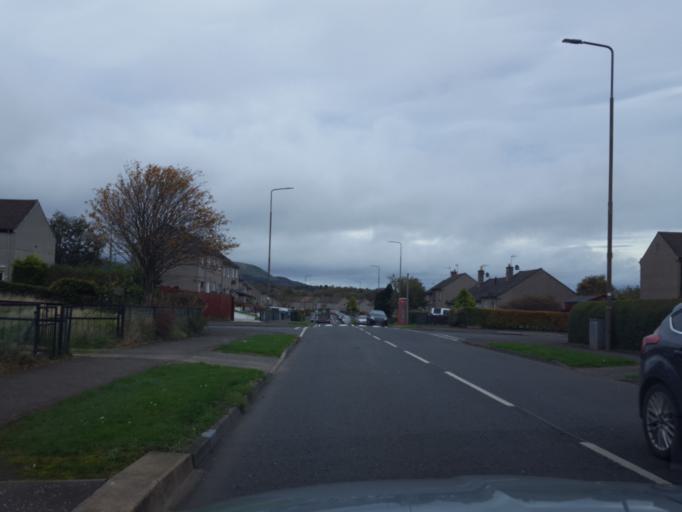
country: GB
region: Scotland
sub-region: Midlothian
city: Penicuik
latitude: 55.8318
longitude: -3.2111
